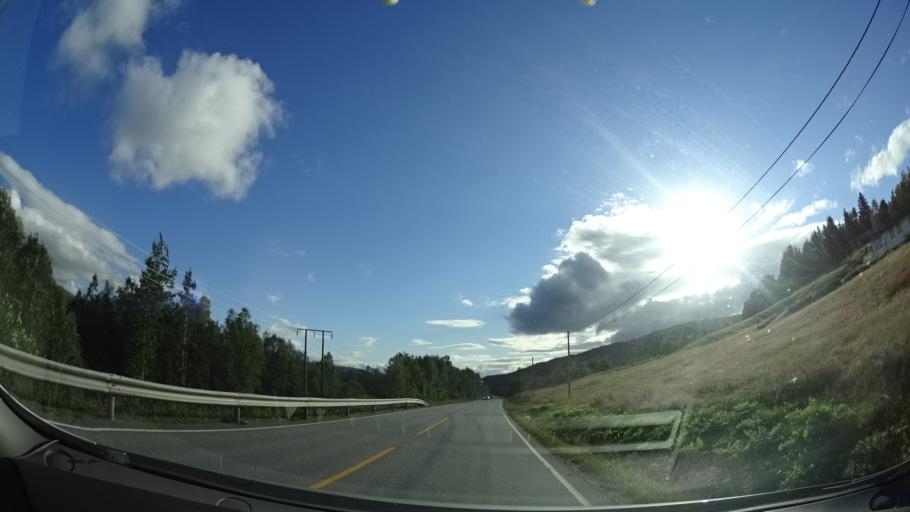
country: NO
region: More og Romsdal
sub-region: Molde
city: Hjelset
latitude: 62.8029
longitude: 7.5718
